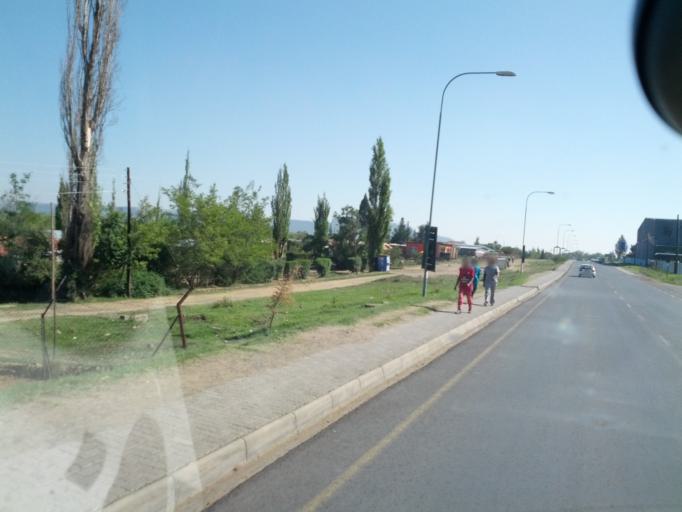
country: LS
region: Maseru
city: Maseru
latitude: -29.3059
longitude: 27.4993
